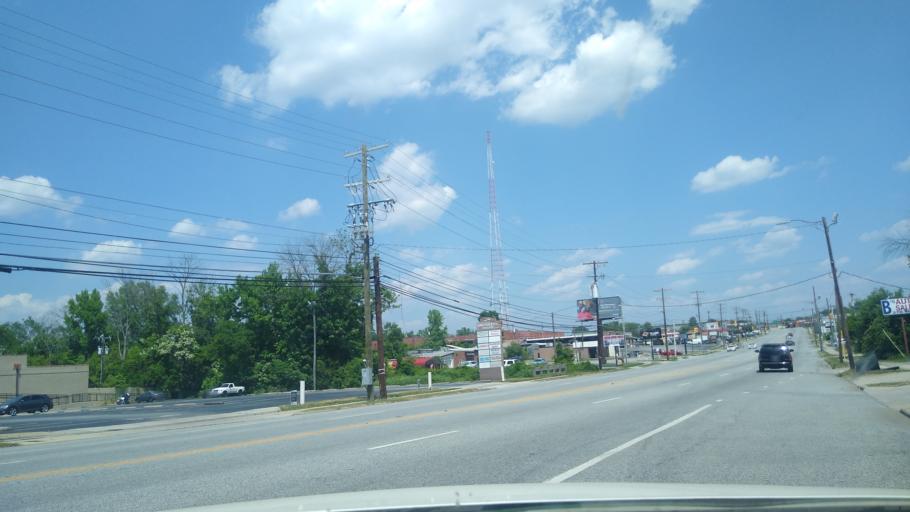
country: US
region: North Carolina
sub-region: Guilford County
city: Greensboro
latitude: 36.0848
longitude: -79.7655
